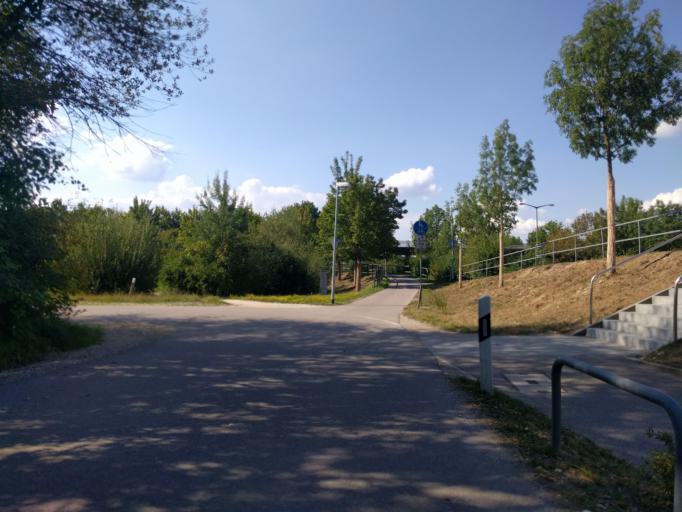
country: DE
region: Bavaria
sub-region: Upper Palatinate
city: Regensburg
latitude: 48.9993
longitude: 12.1309
